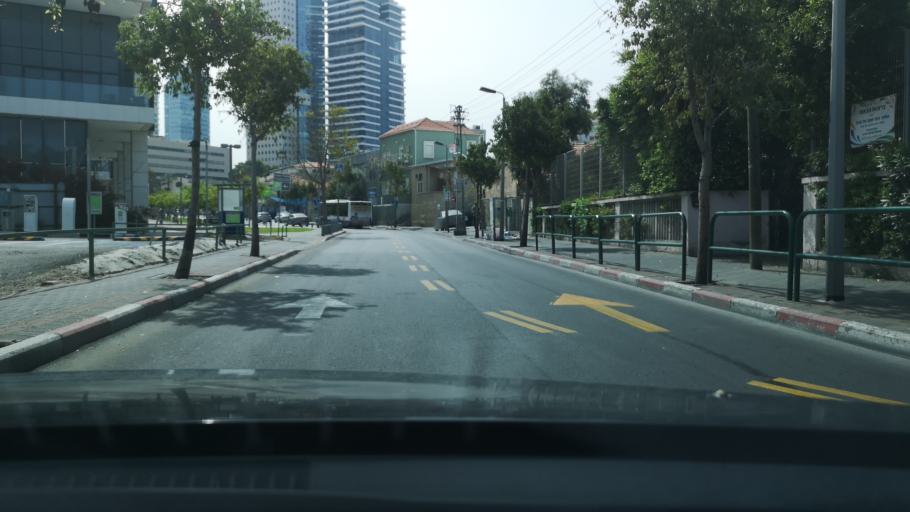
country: IL
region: Tel Aviv
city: Yafo
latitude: 32.0654
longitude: 34.7658
